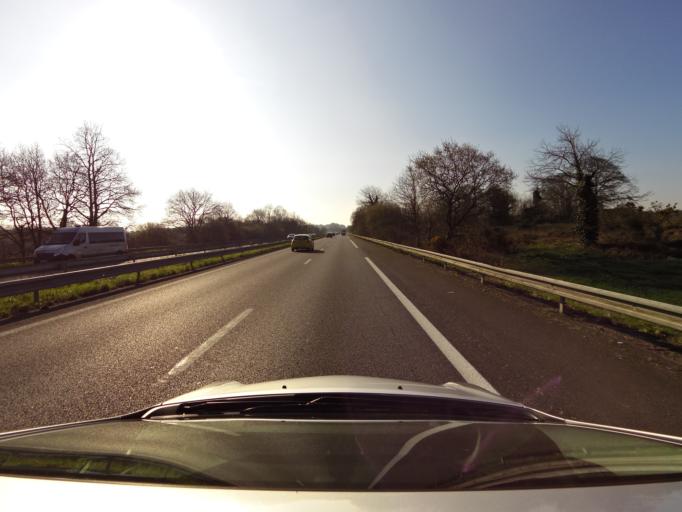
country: FR
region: Brittany
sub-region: Departement du Morbihan
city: Queven
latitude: 47.7845
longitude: -3.4295
